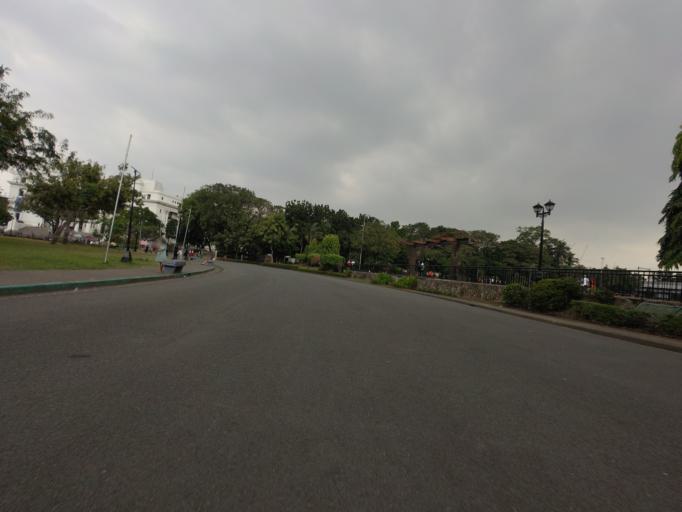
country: PH
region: Metro Manila
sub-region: City of Manila
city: Port Area
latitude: 14.5844
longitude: 120.9821
